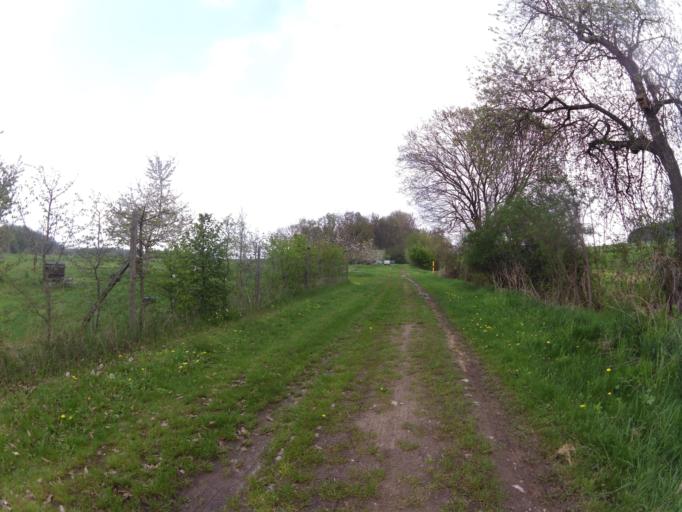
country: DE
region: Bavaria
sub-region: Regierungsbezirk Unterfranken
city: Ochsenfurt
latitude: 49.6999
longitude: 10.0675
